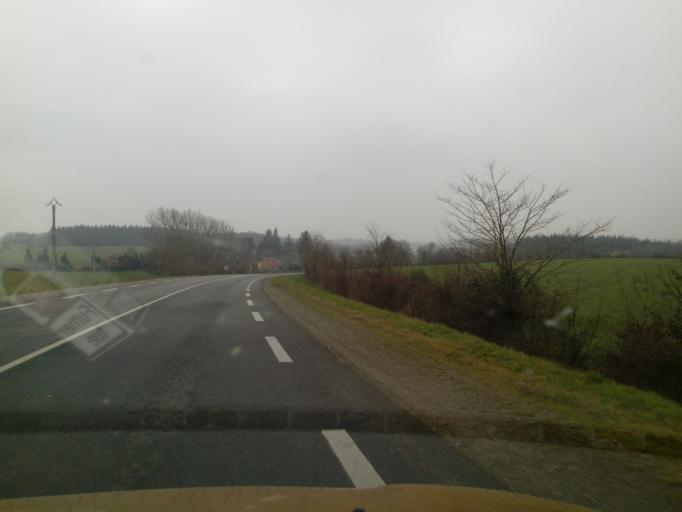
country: FR
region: Brittany
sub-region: Departement du Morbihan
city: Loyat
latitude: 47.9790
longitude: -2.3748
